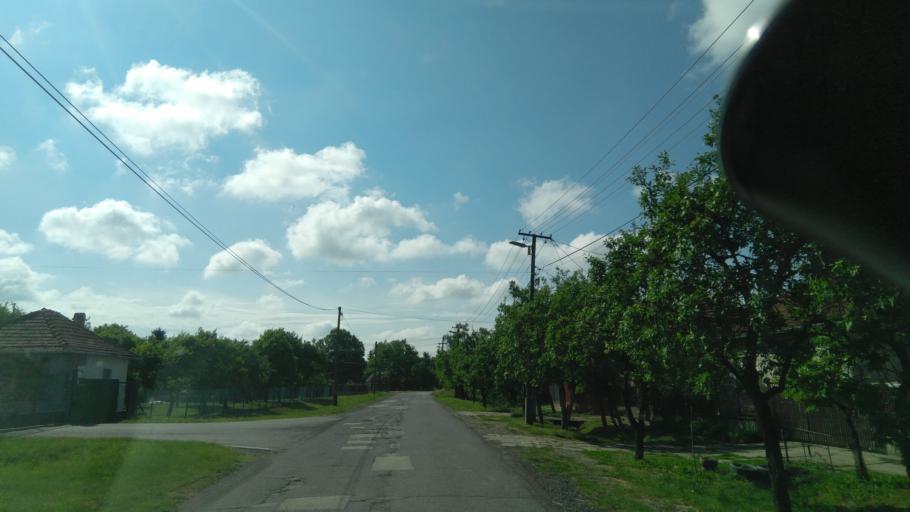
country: HU
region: Bekes
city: Bekes
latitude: 46.7846
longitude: 21.1213
